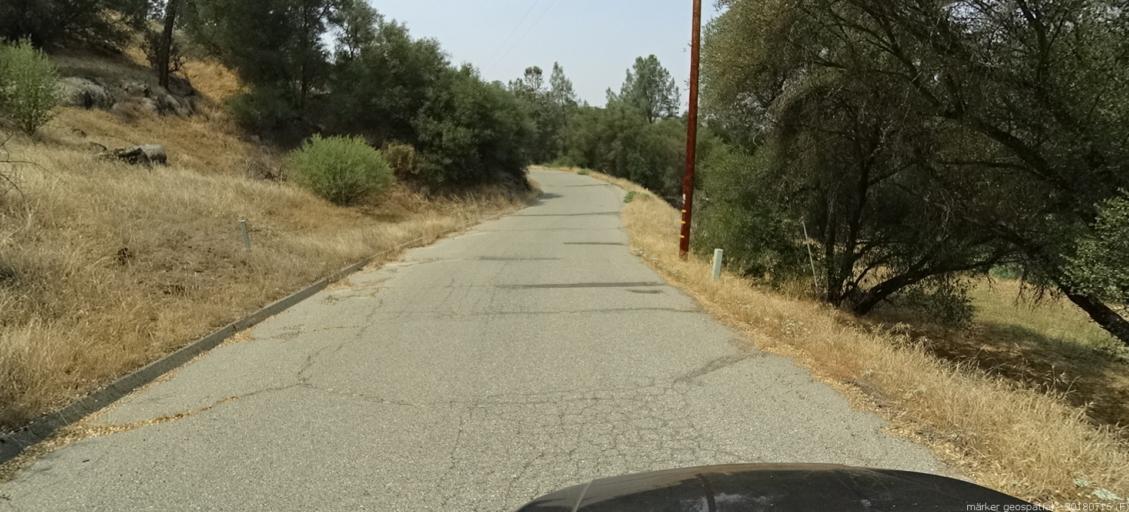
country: US
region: California
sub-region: Madera County
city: Yosemite Lakes
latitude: 37.2329
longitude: -119.7772
